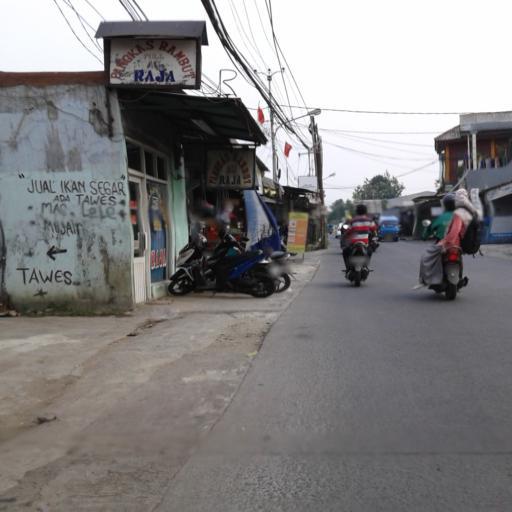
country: ID
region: West Java
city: Sawangan
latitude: -6.3892
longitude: 106.7689
